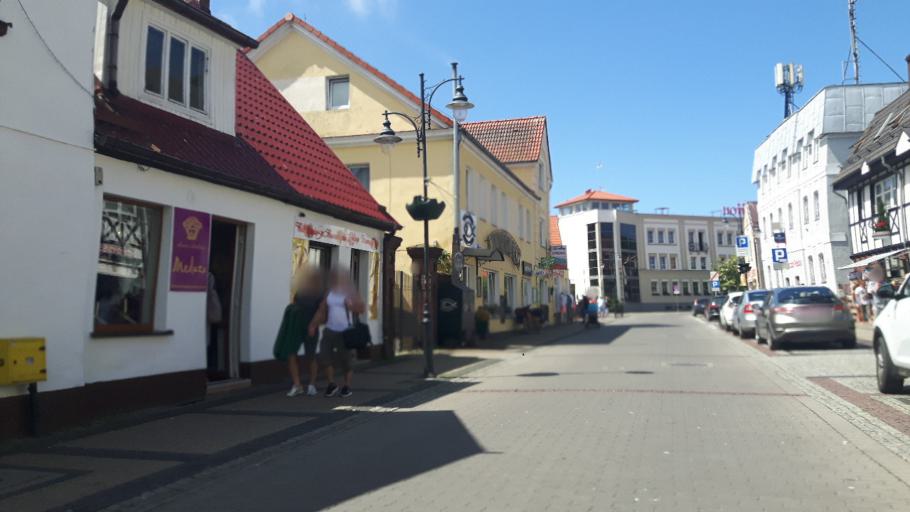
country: PL
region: Pomeranian Voivodeship
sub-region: Powiat slupski
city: Ustka
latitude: 54.5844
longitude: 16.8559
